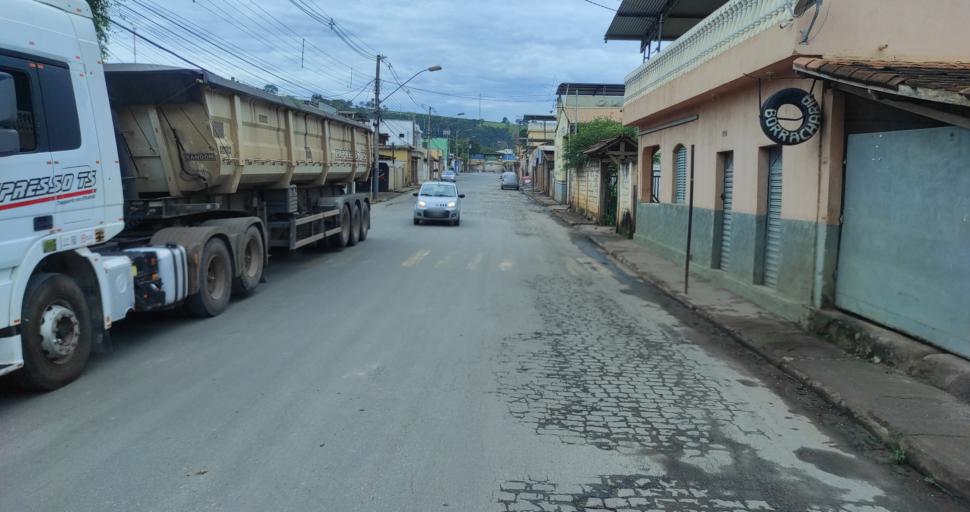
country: BR
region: Minas Gerais
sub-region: Arcos
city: Arcos
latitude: -20.3752
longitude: -45.6636
